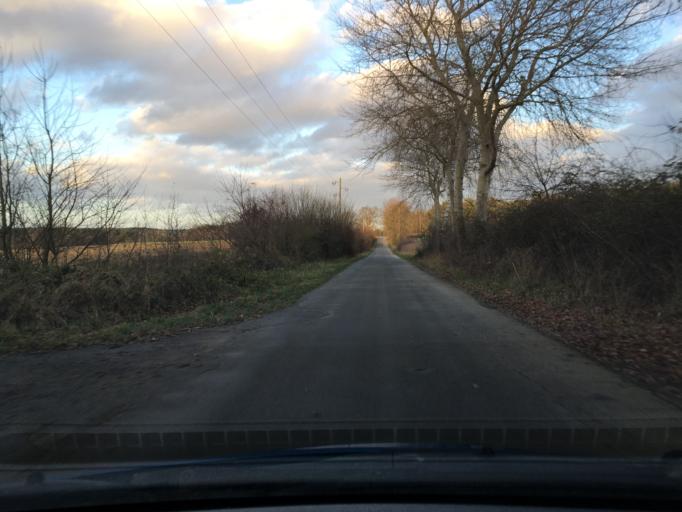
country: DE
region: Lower Saxony
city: Soderstorf
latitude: 53.1297
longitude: 10.1757
